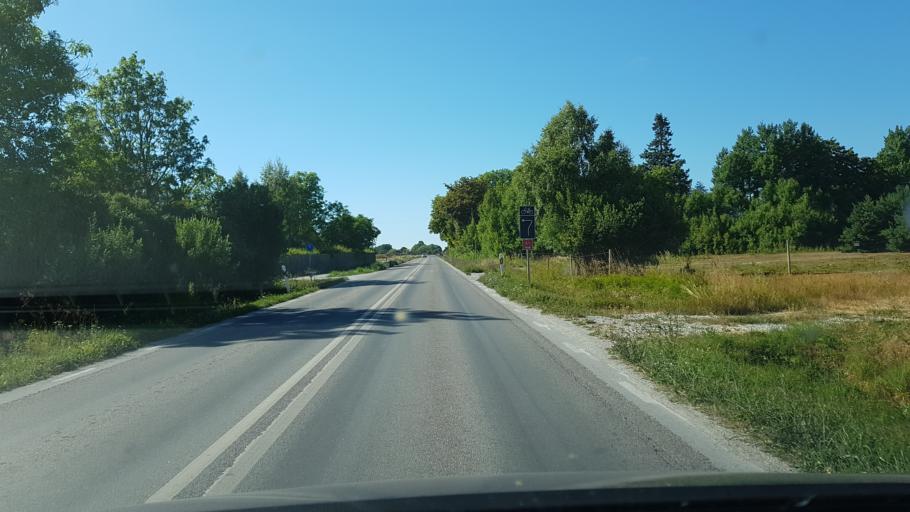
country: SE
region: Gotland
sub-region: Gotland
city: Klintehamn
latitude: 57.4466
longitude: 18.1431
